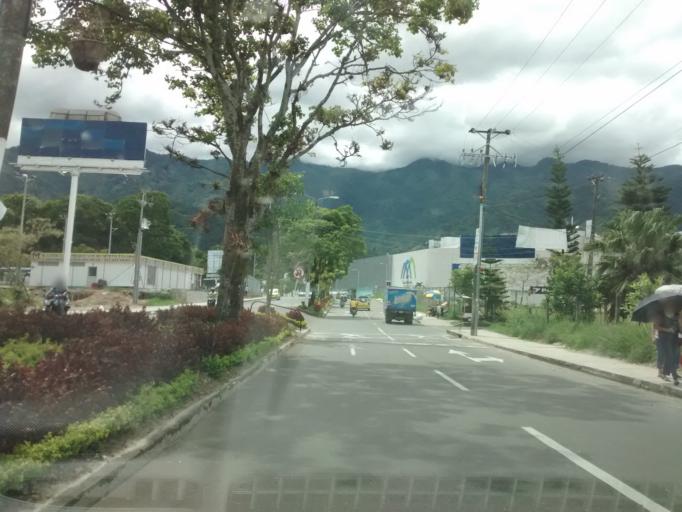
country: CO
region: Tolima
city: Ibague
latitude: 4.4433
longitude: -75.2048
